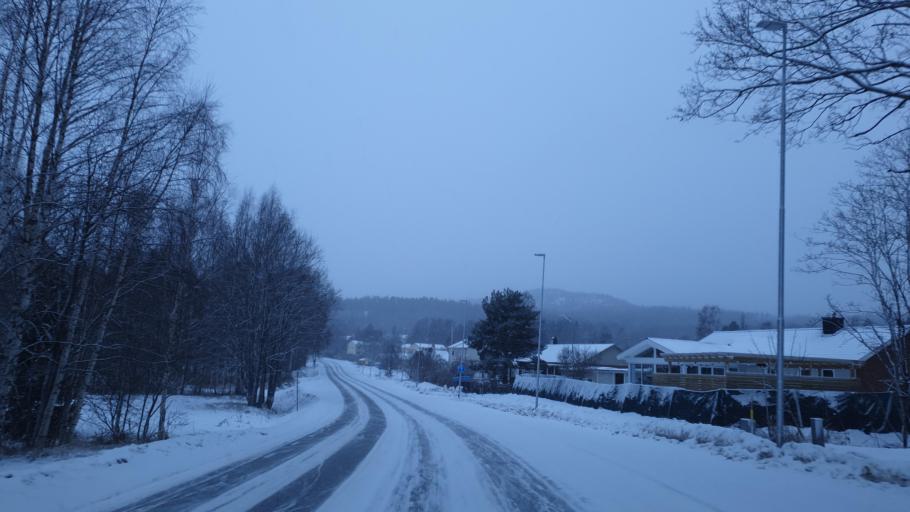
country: SE
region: Vaesternorrland
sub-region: OErnskoeldsviks Kommun
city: Ornskoldsvik
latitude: 63.2998
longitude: 18.6425
